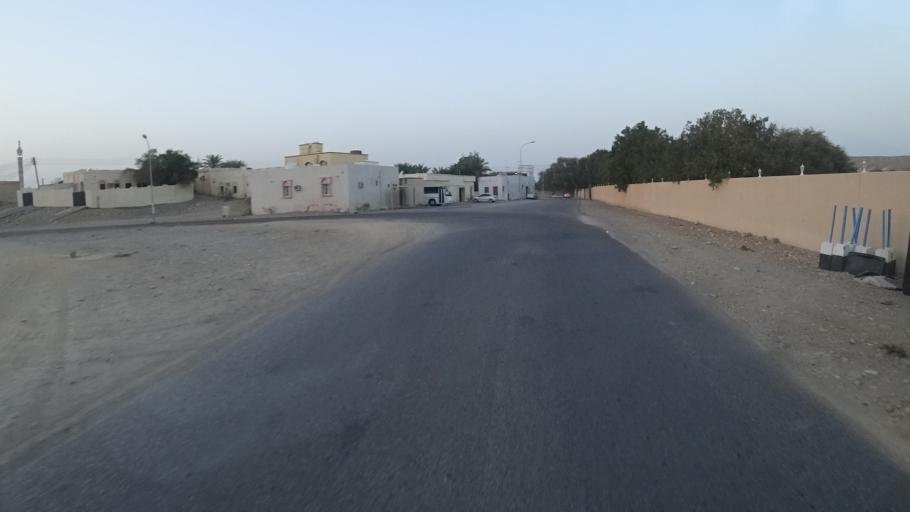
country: OM
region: Ash Sharqiyah
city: Sur
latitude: 22.5396
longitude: 59.4871
